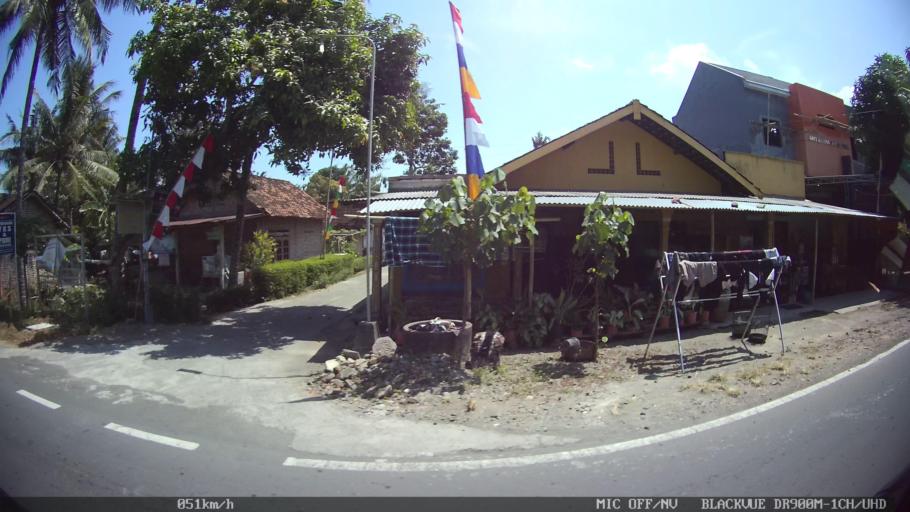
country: ID
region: Daerah Istimewa Yogyakarta
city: Srandakan
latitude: -7.9371
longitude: 110.2580
